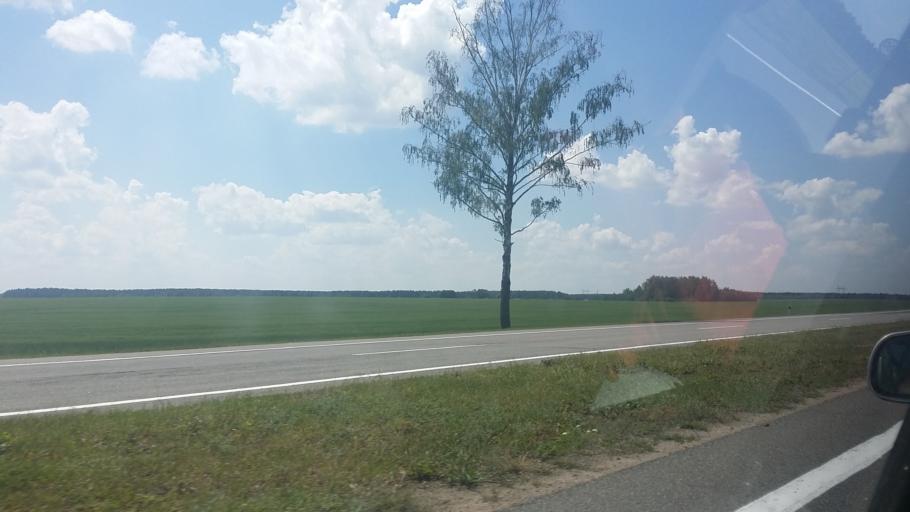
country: BY
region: Minsk
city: Smilavichy
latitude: 53.7642
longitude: 28.1414
